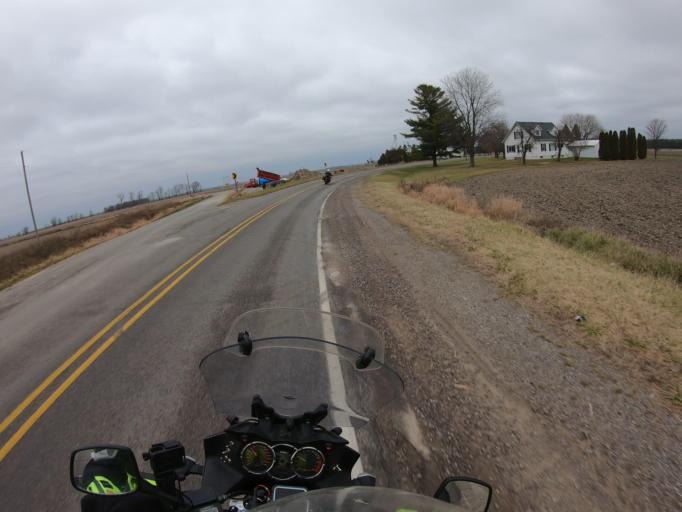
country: US
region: Michigan
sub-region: Saginaw County
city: Burt
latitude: 43.2483
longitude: -83.9862
